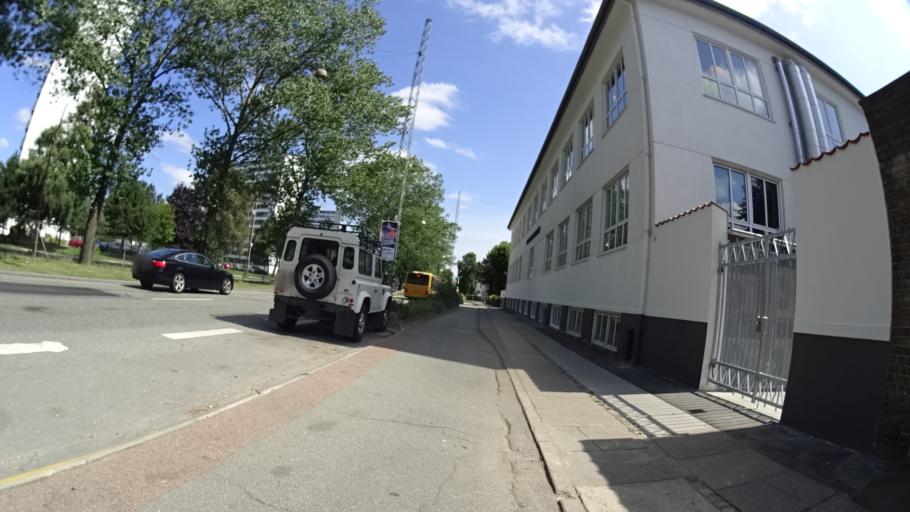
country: DK
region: Central Jutland
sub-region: Arhus Kommune
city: Arhus
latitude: 56.1405
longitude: 10.1982
